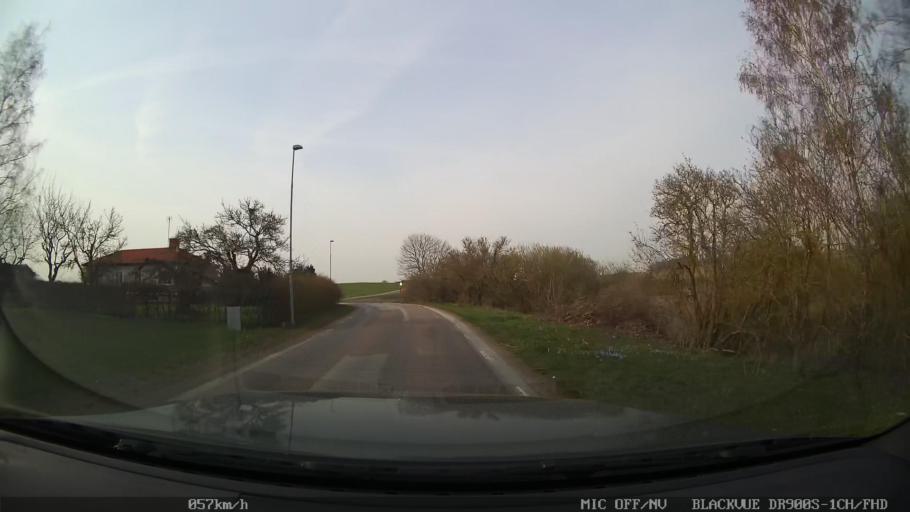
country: SE
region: Skane
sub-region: Ystads Kommun
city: Ystad
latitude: 55.4472
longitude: 13.8330
